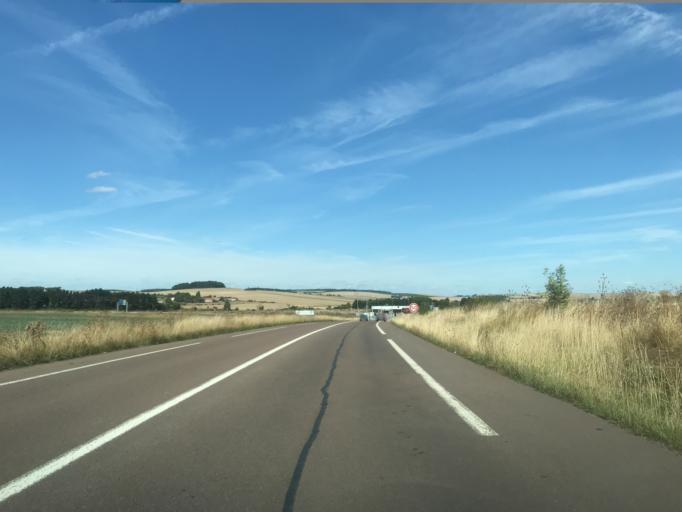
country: FR
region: Champagne-Ardenne
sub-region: Departement de la Marne
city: Chatillon-sur-Marne
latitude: 49.1511
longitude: 3.7151
